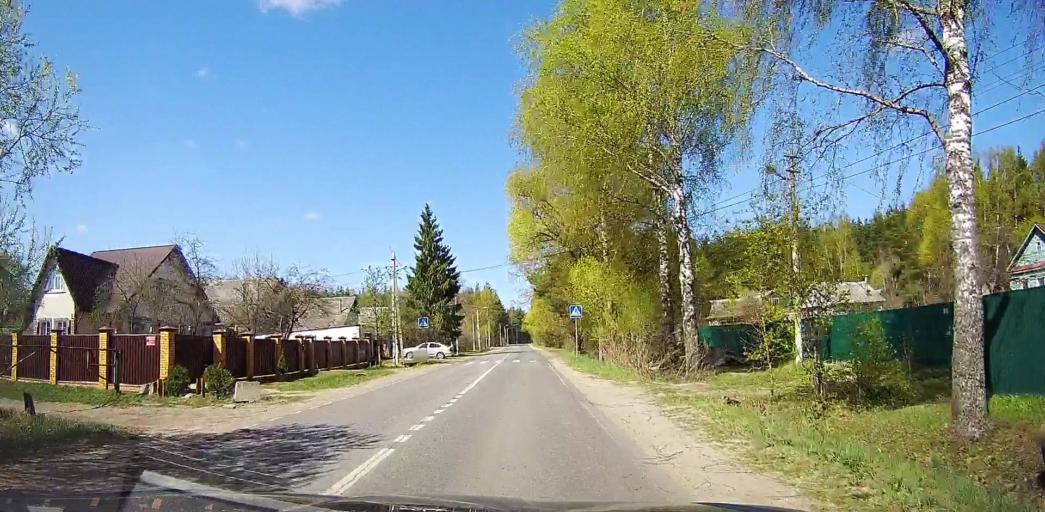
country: RU
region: Moskovskaya
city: Ramenskoye
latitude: 55.6119
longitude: 38.2855
